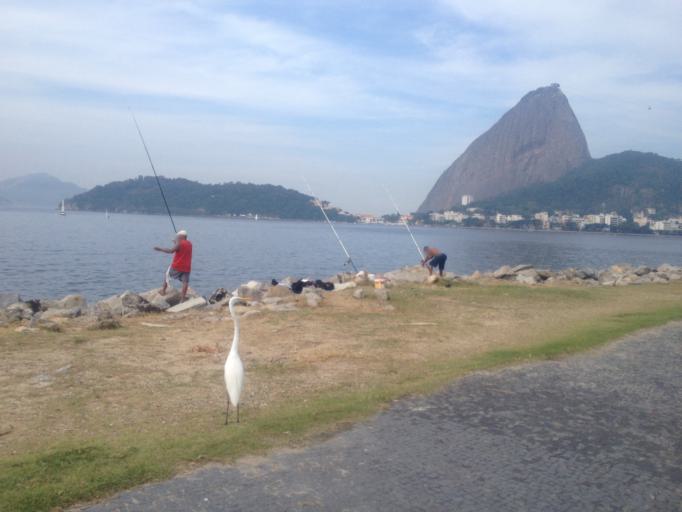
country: BR
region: Rio de Janeiro
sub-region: Rio De Janeiro
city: Rio de Janeiro
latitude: -22.9369
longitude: -43.1688
